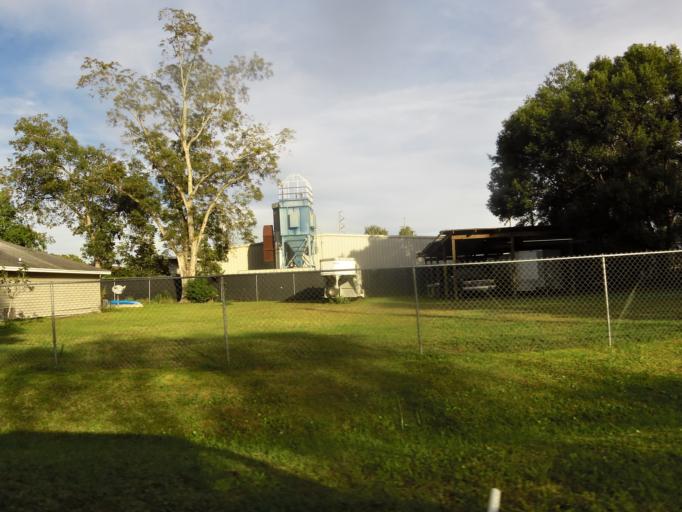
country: US
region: Florida
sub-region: Duval County
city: Jacksonville
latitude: 30.4105
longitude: -81.6520
